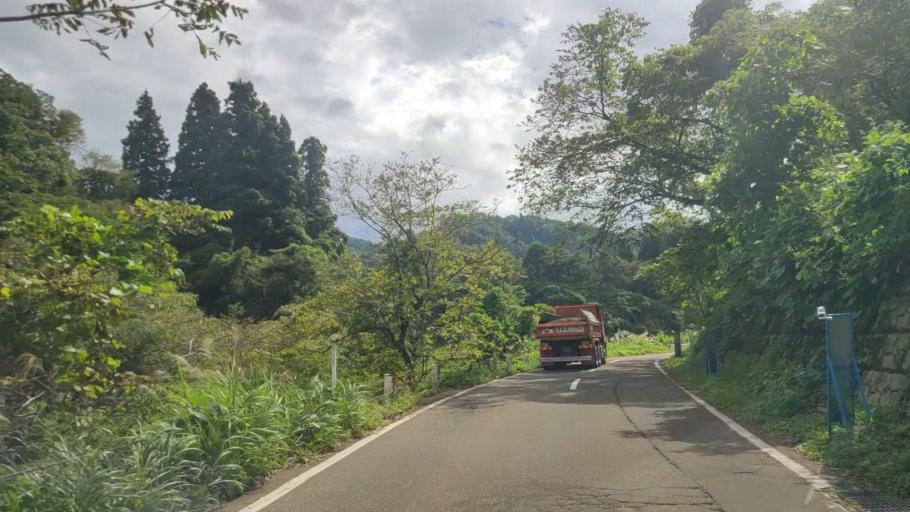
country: JP
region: Niigata
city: Arai
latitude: 36.9471
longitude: 138.2874
